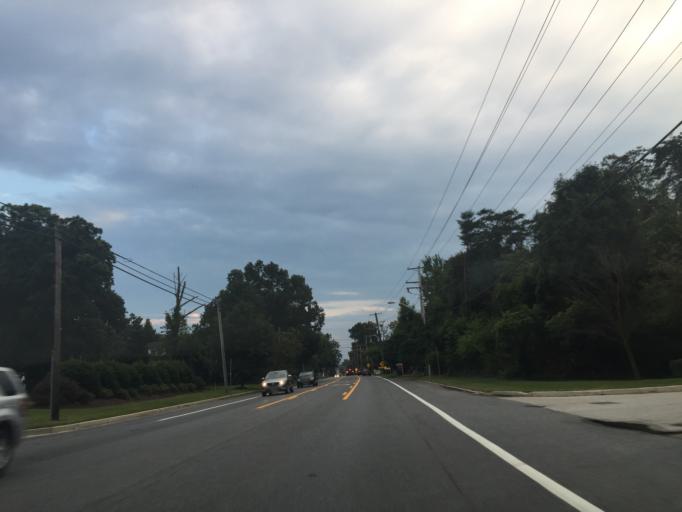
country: US
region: Maryland
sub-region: Anne Arundel County
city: Severn
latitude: 39.1201
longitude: -76.6906
